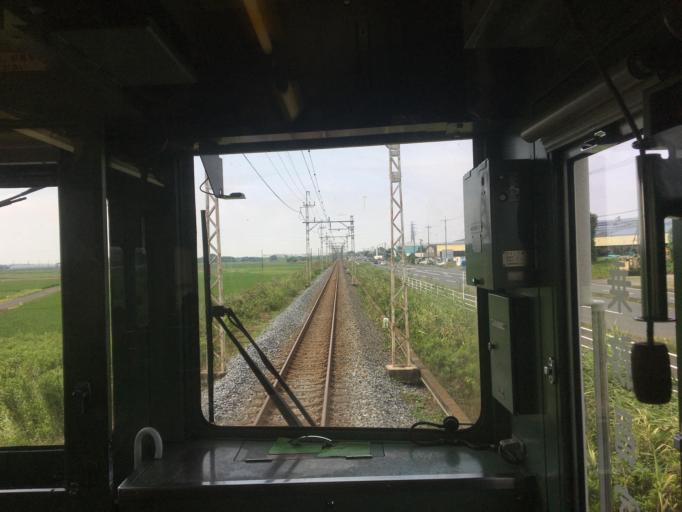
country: JP
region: Tochigi
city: Sano
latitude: 36.2850
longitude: 139.5618
